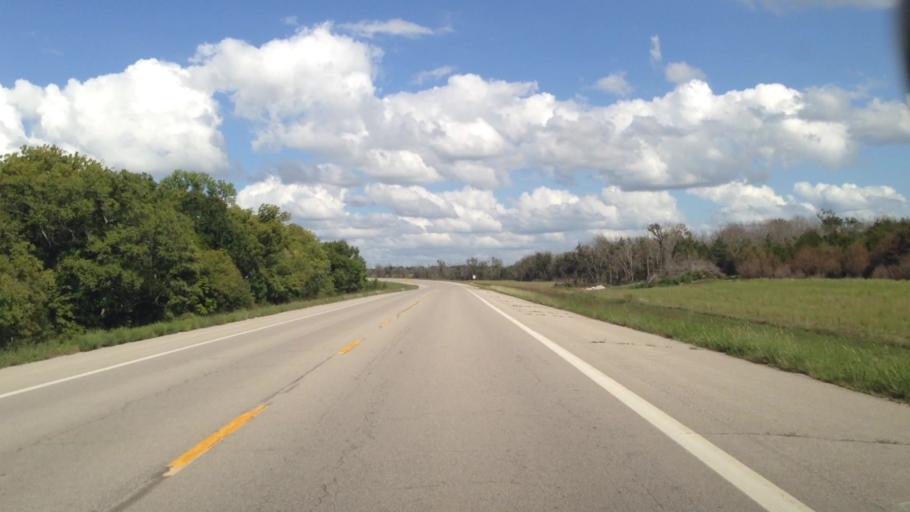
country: US
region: Kansas
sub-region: Neosho County
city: Erie
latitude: 37.6887
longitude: -95.1689
